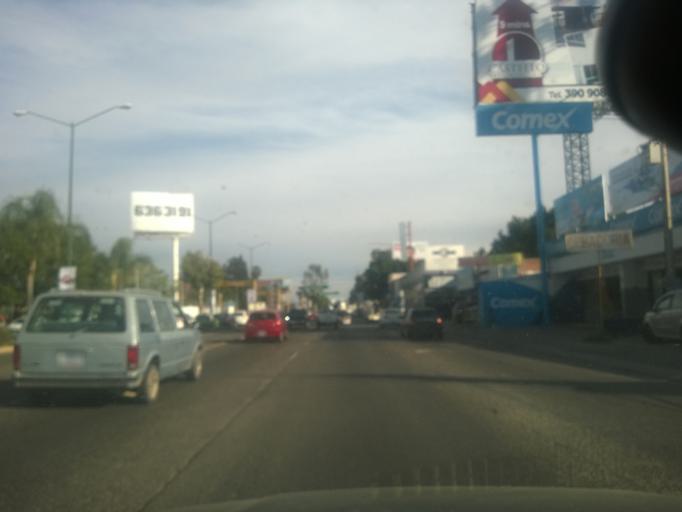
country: MX
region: Guanajuato
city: Leon
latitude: 21.1113
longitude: -101.6477
